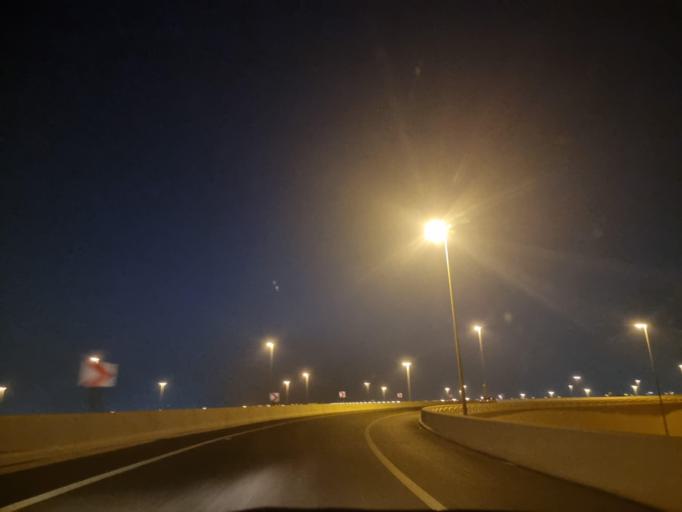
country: AE
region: Abu Dhabi
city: Abu Dhabi
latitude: 24.4167
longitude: 54.7642
